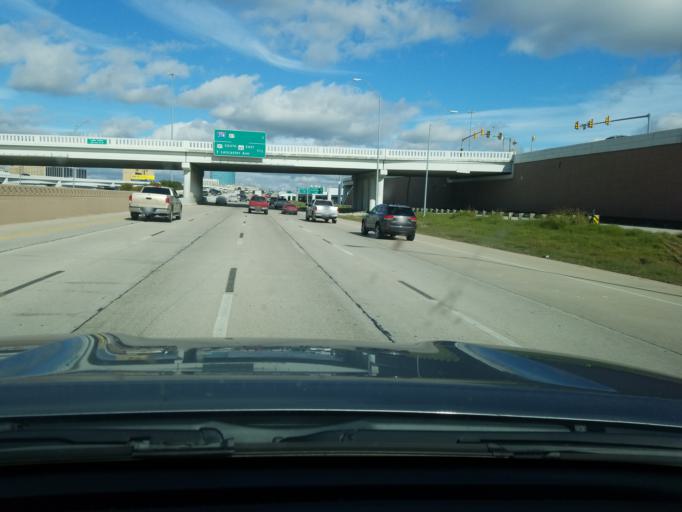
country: US
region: Texas
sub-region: Tarrant County
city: Fort Worth
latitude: 32.7418
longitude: -97.3428
